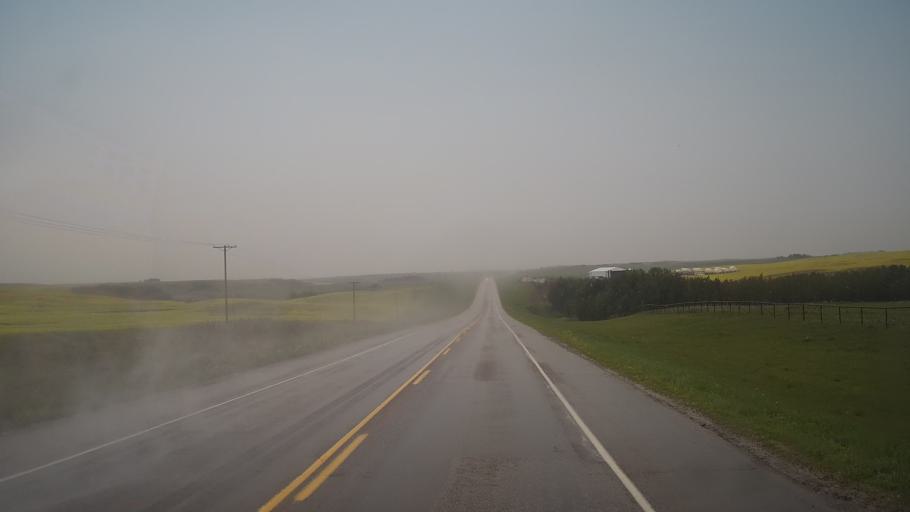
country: CA
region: Saskatchewan
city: Biggar
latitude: 52.0687
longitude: -108.0065
